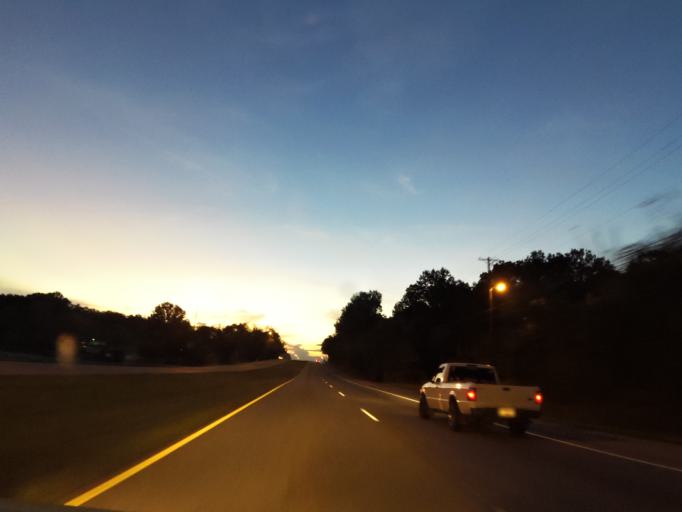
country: US
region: Tennessee
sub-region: Knox County
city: Mascot
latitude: 36.0208
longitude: -83.7849
